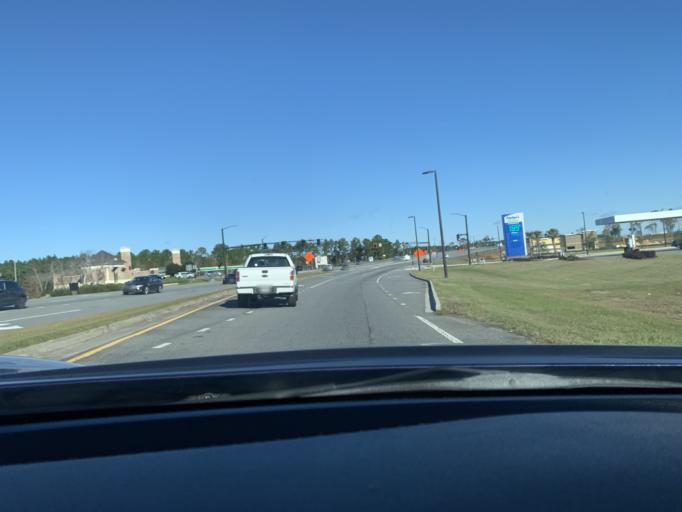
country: US
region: Georgia
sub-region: Chatham County
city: Pooler
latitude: 32.0787
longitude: -81.2816
